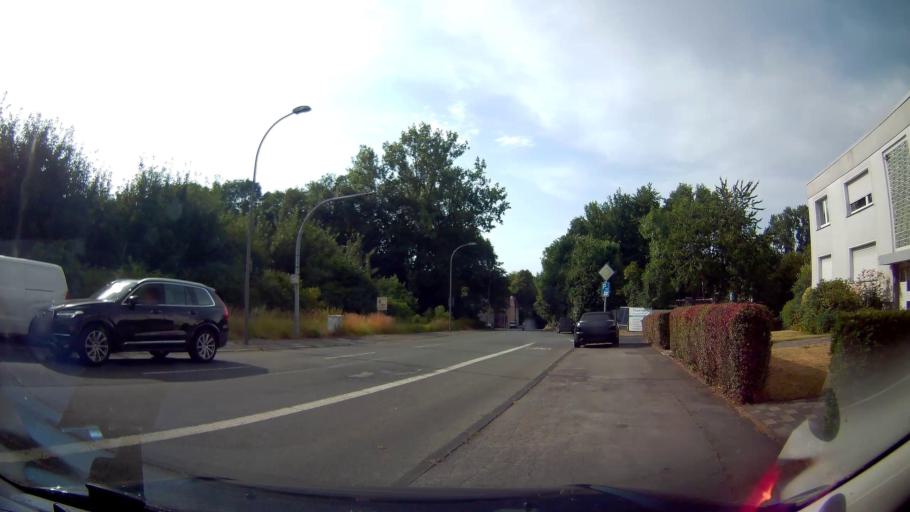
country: DE
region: North Rhine-Westphalia
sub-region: Regierungsbezirk Arnsberg
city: Herne
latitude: 51.5210
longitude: 7.2502
